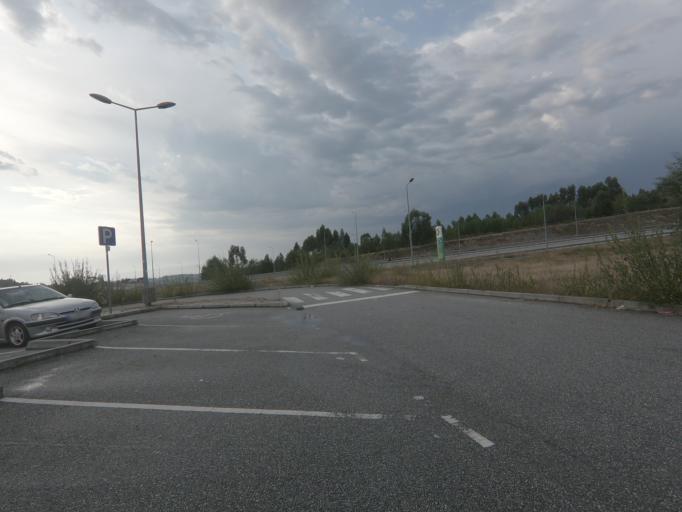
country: PT
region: Viseu
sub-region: Viseu
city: Campo
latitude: 40.7080
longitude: -7.9432
